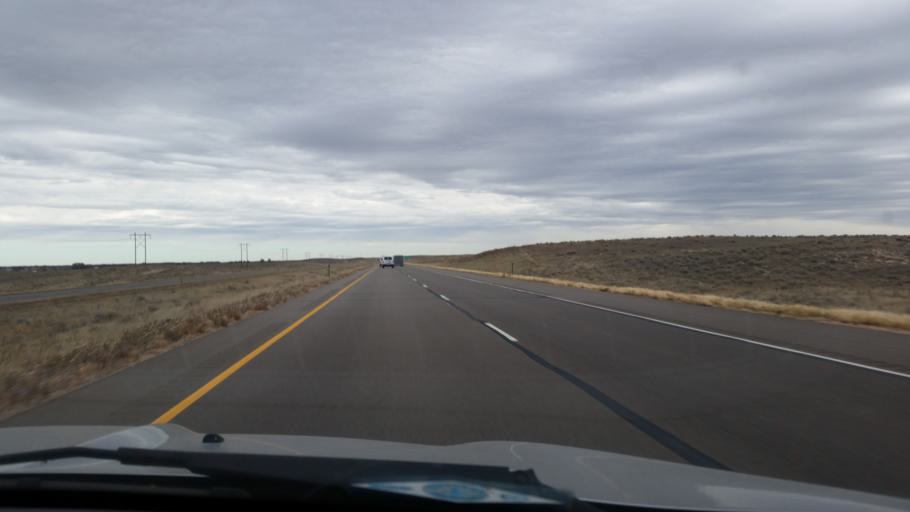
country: US
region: Colorado
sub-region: Morgan County
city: Brush
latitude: 40.3469
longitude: -103.4489
